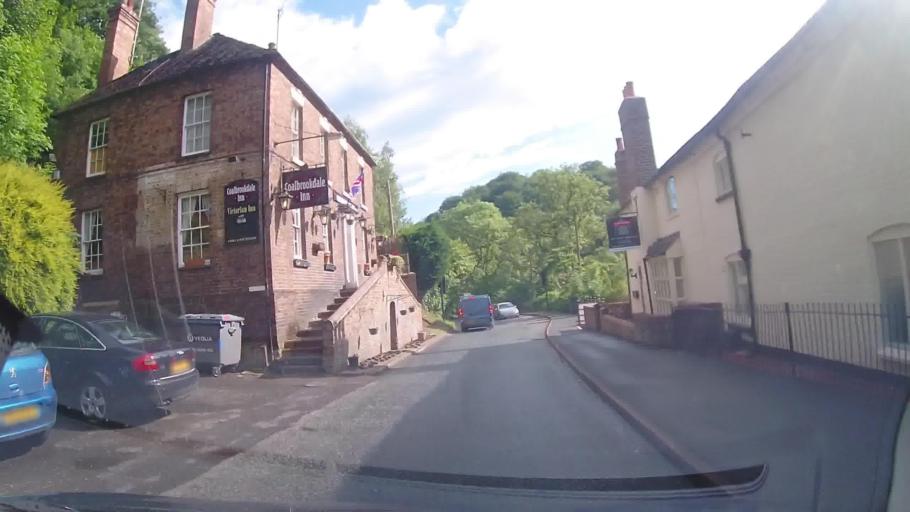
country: GB
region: England
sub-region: Telford and Wrekin
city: Ironbridge
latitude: 52.6394
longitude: -2.4917
